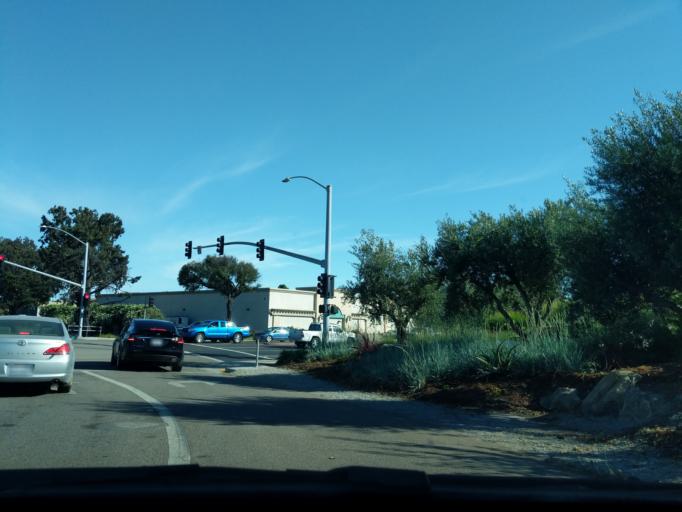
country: US
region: California
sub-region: San Luis Obispo County
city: San Luis Obispo
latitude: 35.2648
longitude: -120.6759
